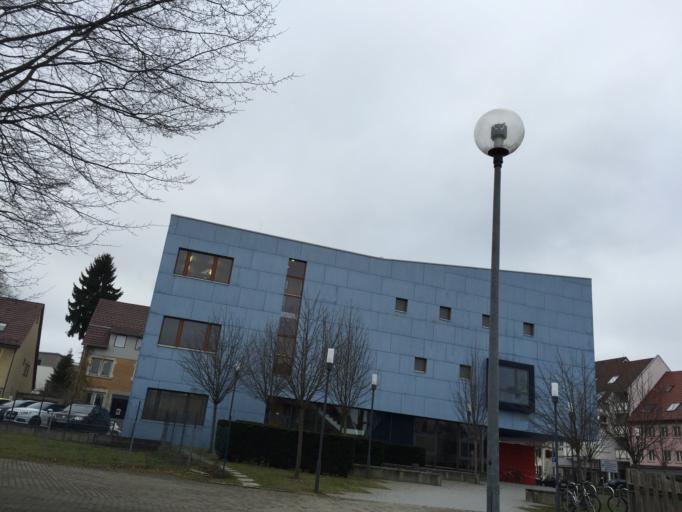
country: DE
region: Baden-Wuerttemberg
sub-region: Freiburg Region
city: Trossingen
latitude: 48.0760
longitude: 8.6377
